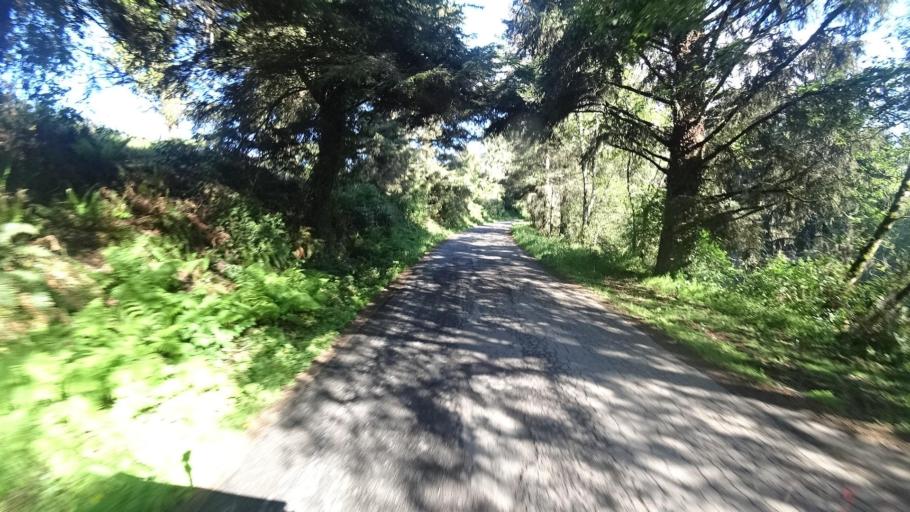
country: US
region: California
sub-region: Humboldt County
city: Westhaven-Moonstone
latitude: 41.0061
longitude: -124.1065
